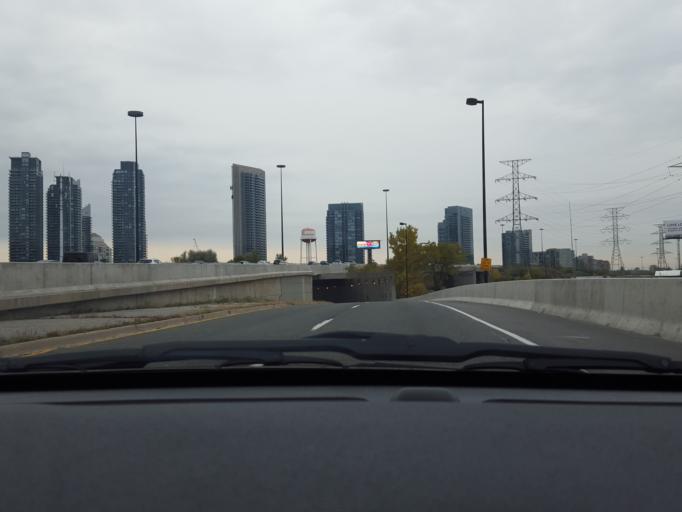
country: CA
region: Ontario
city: Etobicoke
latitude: 43.6294
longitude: -79.4794
